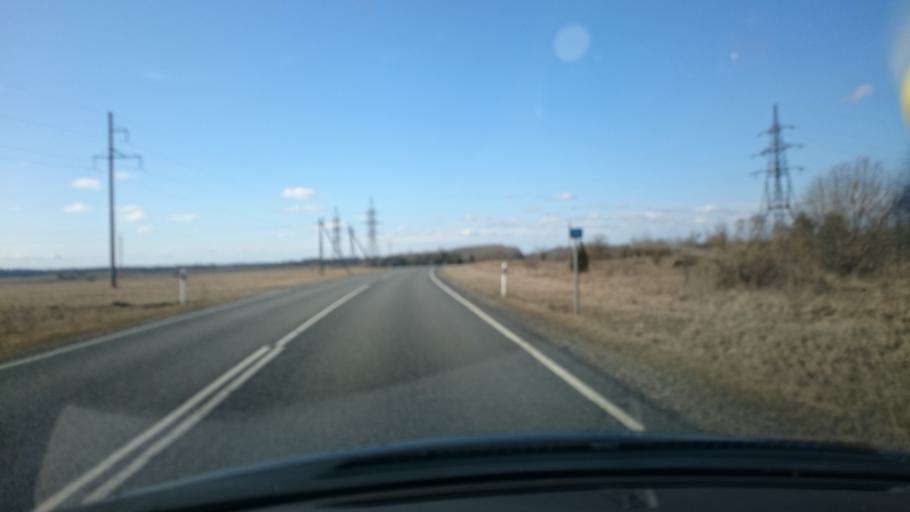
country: EE
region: Laeaene
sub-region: Lihula vald
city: Lihula
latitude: 58.6766
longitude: 23.8174
